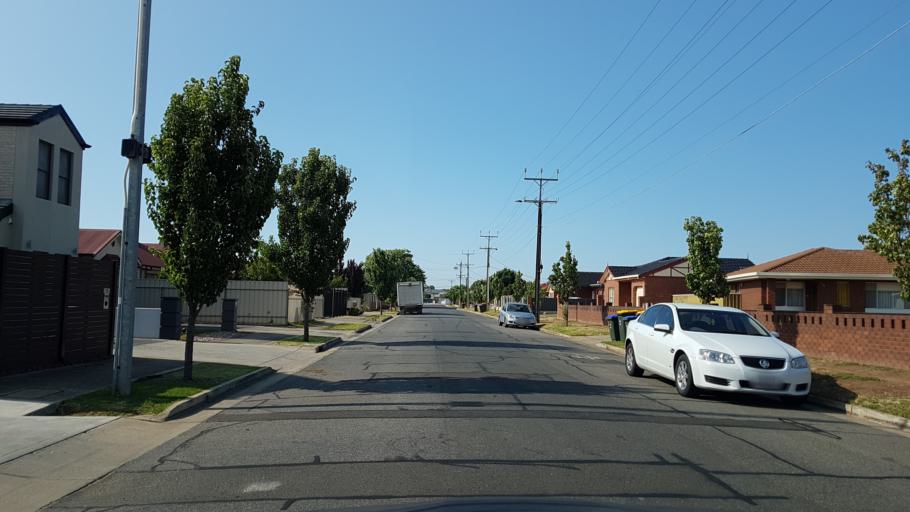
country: AU
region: South Australia
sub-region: Charles Sturt
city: Findon
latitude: -34.9042
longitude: 138.5275
